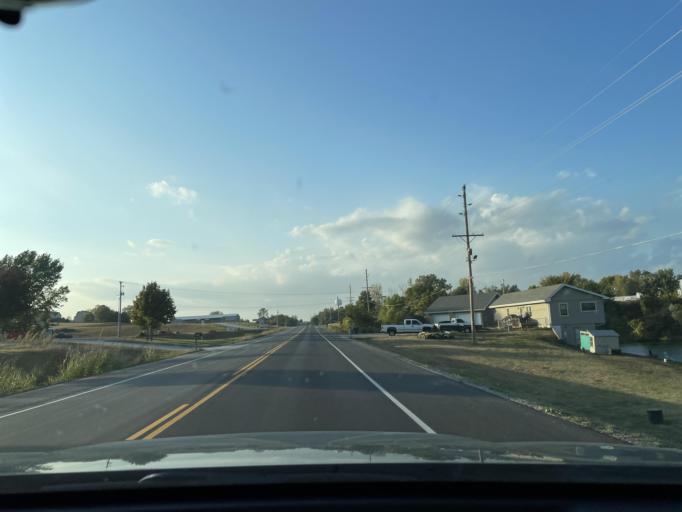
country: US
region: Missouri
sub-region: Andrew County
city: Country Club Village
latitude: 39.8234
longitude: -94.8516
